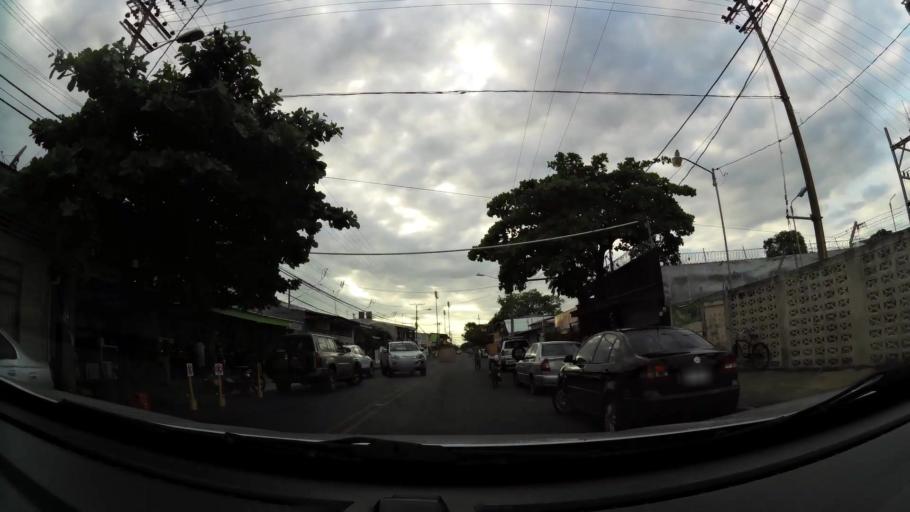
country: CR
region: Puntarenas
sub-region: Canton Central de Puntarenas
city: Puntarenas
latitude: 9.9770
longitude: -84.8370
